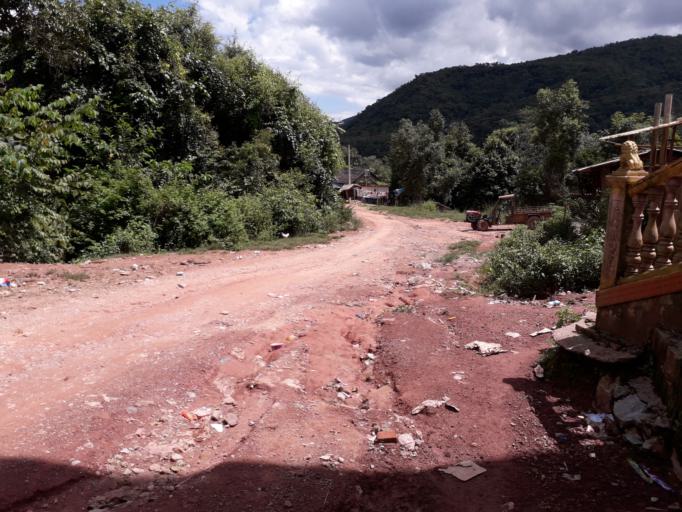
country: CN
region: Yunnan
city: Menglie
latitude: 22.2661
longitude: 101.5731
